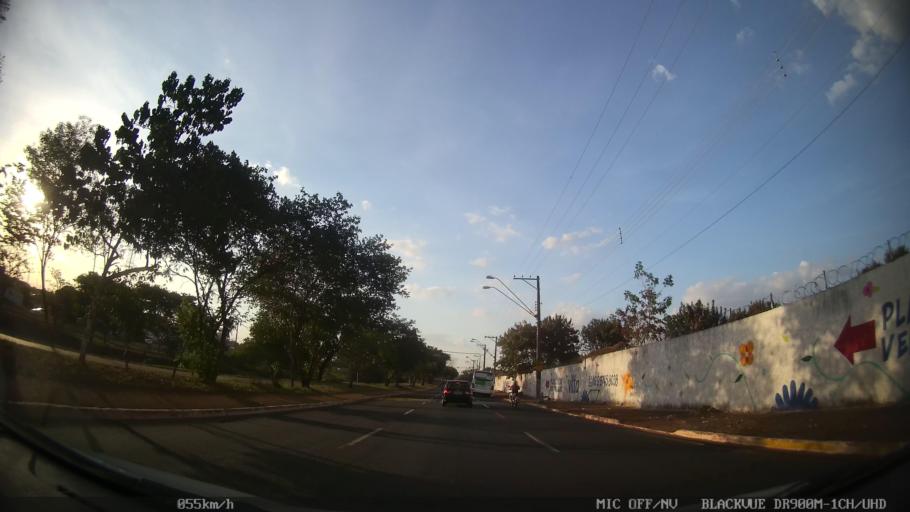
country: BR
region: Sao Paulo
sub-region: Ribeirao Preto
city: Ribeirao Preto
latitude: -21.1298
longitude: -47.8030
